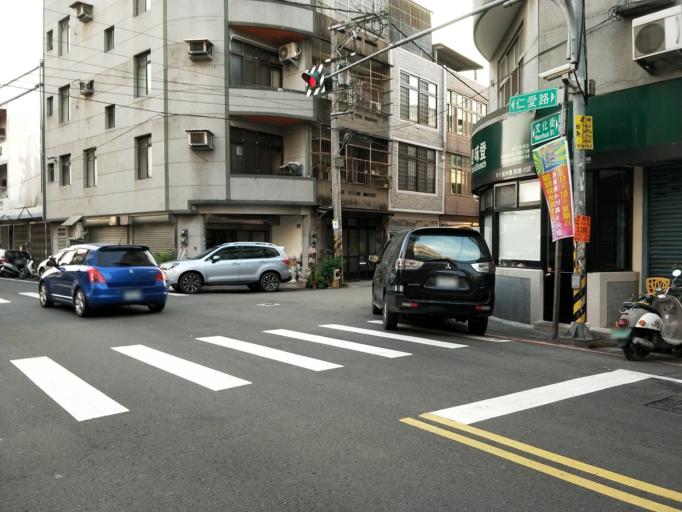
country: TW
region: Taiwan
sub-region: Hsinchu
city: Zhubei
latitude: 24.8270
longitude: 121.0808
